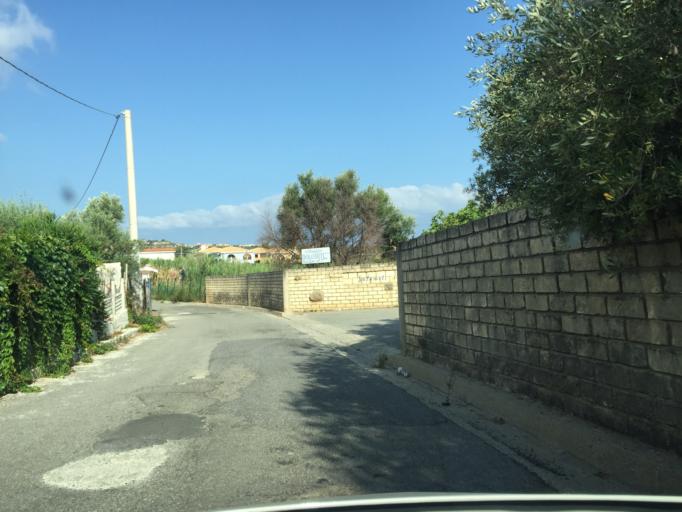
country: IT
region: Calabria
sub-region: Provincia di Vibo-Valentia
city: Pannaconi
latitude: 38.7182
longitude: 16.0576
